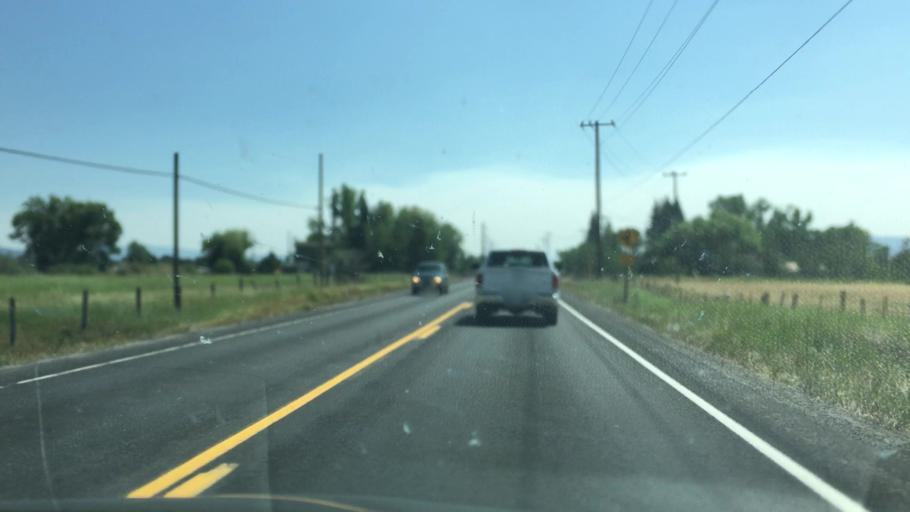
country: US
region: Idaho
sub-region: Valley County
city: McCall
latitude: 44.8677
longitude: -116.0908
